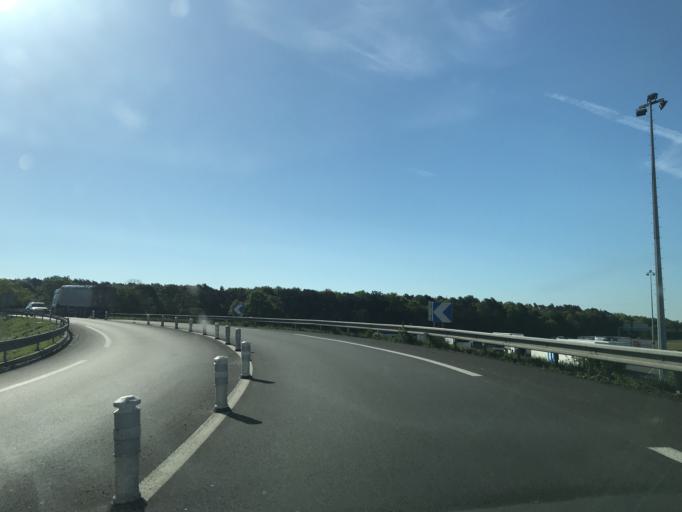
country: FR
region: Centre
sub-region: Departement du Loiret
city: Saran
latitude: 47.9506
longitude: 1.8470
